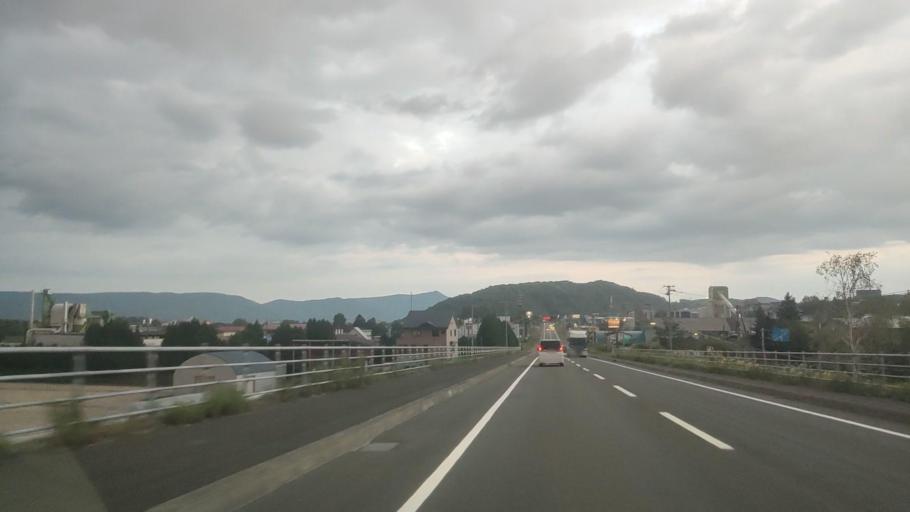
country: JP
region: Hokkaido
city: Shimo-furano
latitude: 43.3526
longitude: 142.3657
